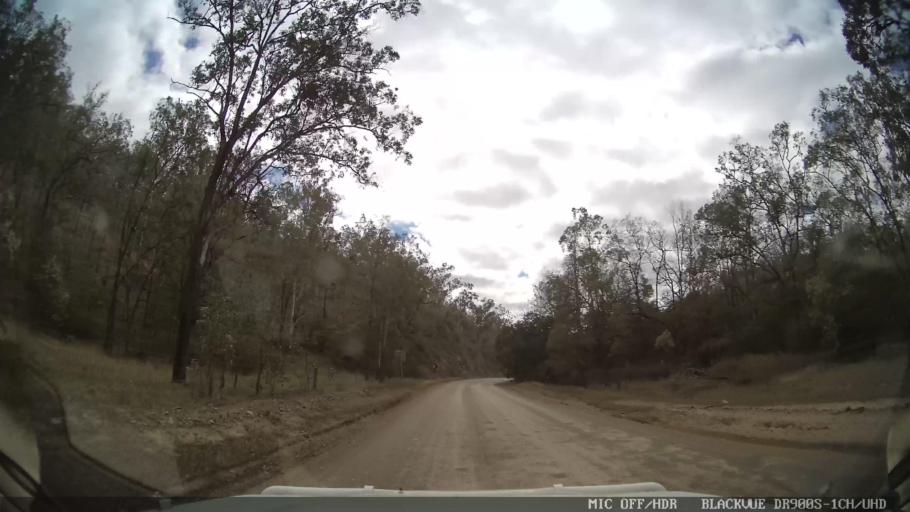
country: AU
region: Queensland
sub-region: Gladstone
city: Toolooa
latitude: -24.6292
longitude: 151.2814
